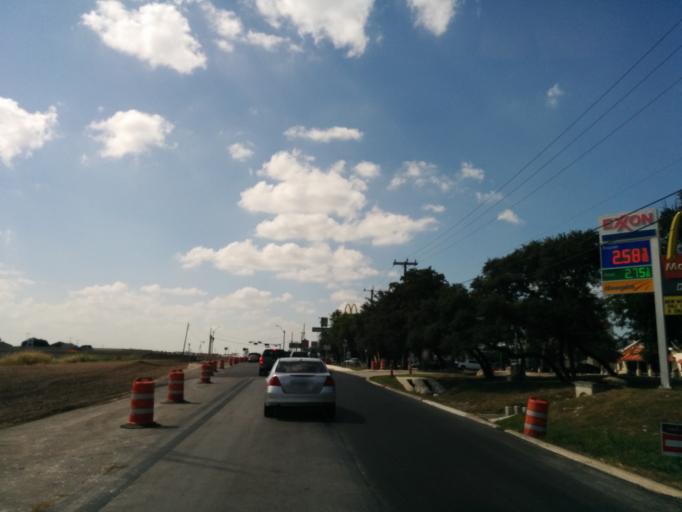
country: US
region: Texas
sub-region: Bexar County
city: Cross Mountain
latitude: 29.6749
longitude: -98.6344
